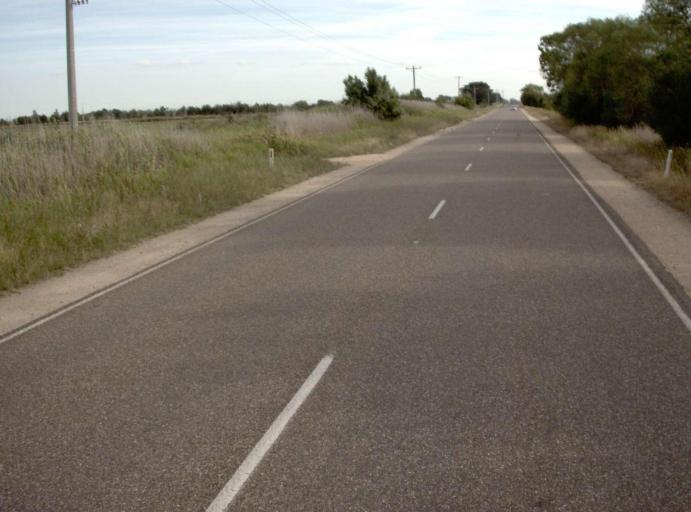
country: AU
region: Victoria
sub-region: Wellington
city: Heyfield
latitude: -37.9787
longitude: 146.8886
